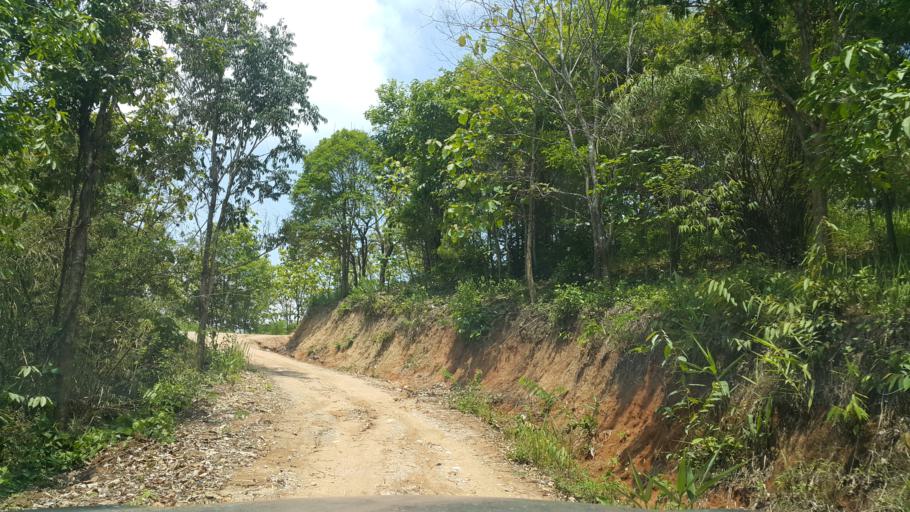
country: TH
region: Chiang Rai
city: Chiang Rai
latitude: 19.9989
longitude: 99.7188
